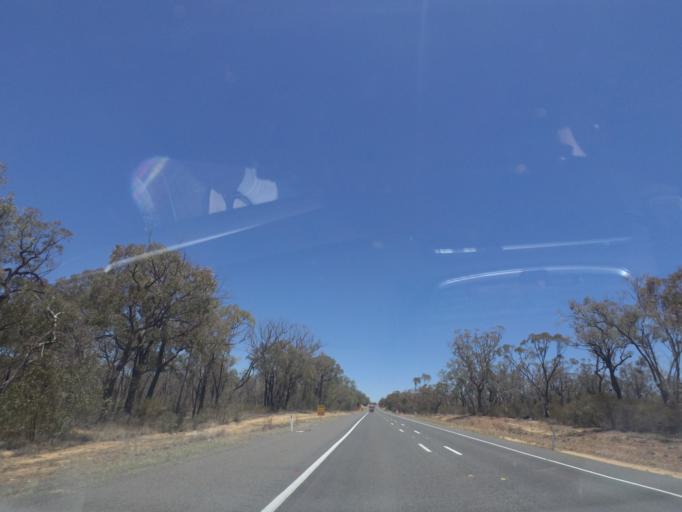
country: AU
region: New South Wales
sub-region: Warrumbungle Shire
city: Coonabarabran
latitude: -30.9139
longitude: 149.4350
